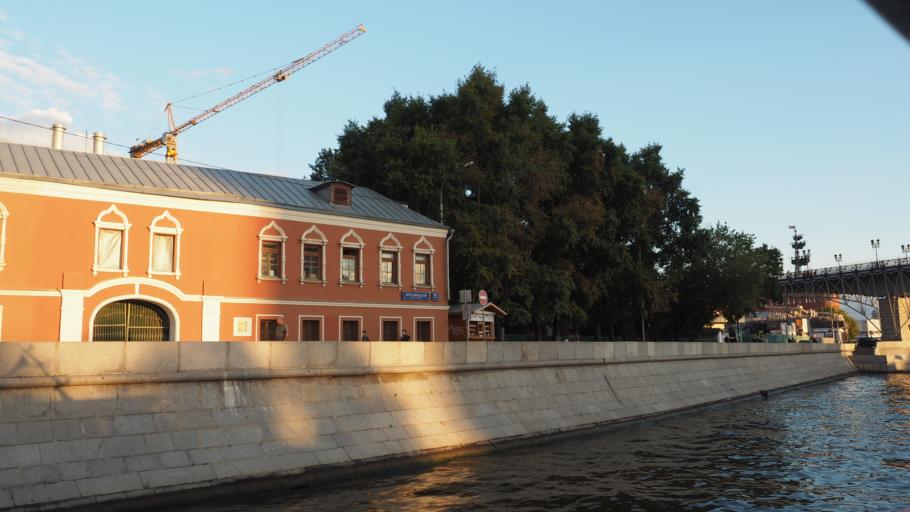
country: RU
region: Moscow
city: Moscow
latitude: 55.7445
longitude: 37.6097
